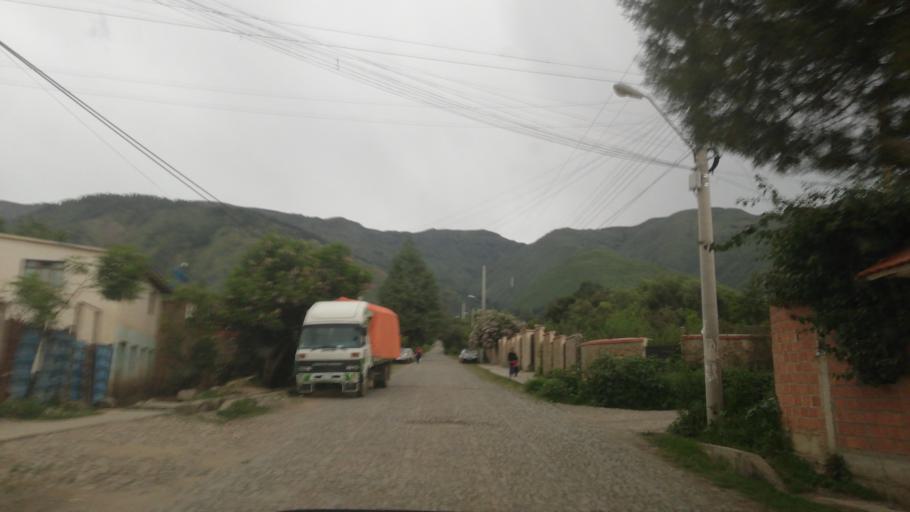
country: BO
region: Cochabamba
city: Cochabamba
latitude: -17.3298
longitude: -66.2152
